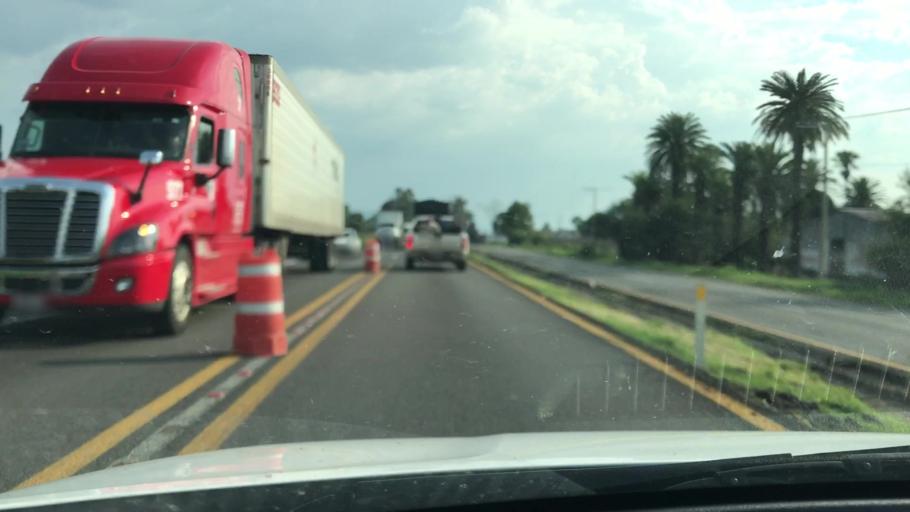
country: MX
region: Guanajuato
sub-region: Irapuato
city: San Ignacio de Rivera (Ojo de Agua)
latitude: 20.5109
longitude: -101.4707
